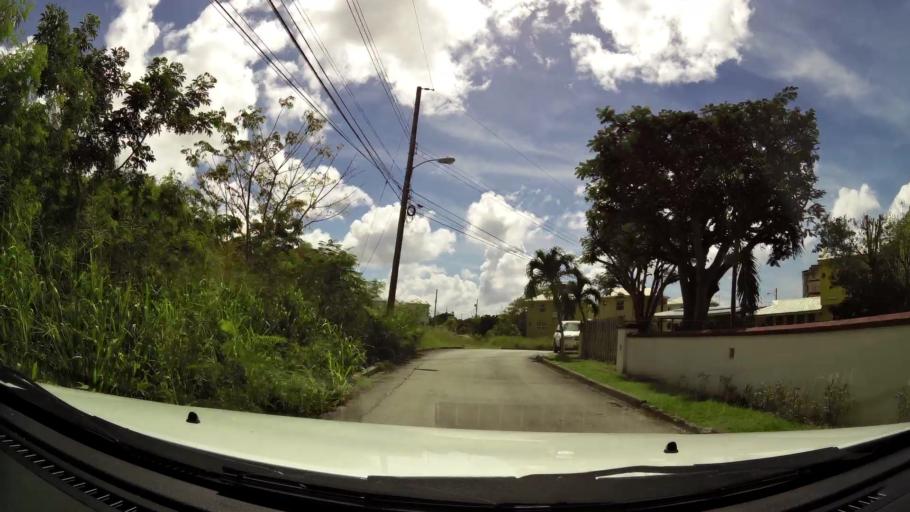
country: BB
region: Saint James
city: Holetown
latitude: 13.1450
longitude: -59.6282
